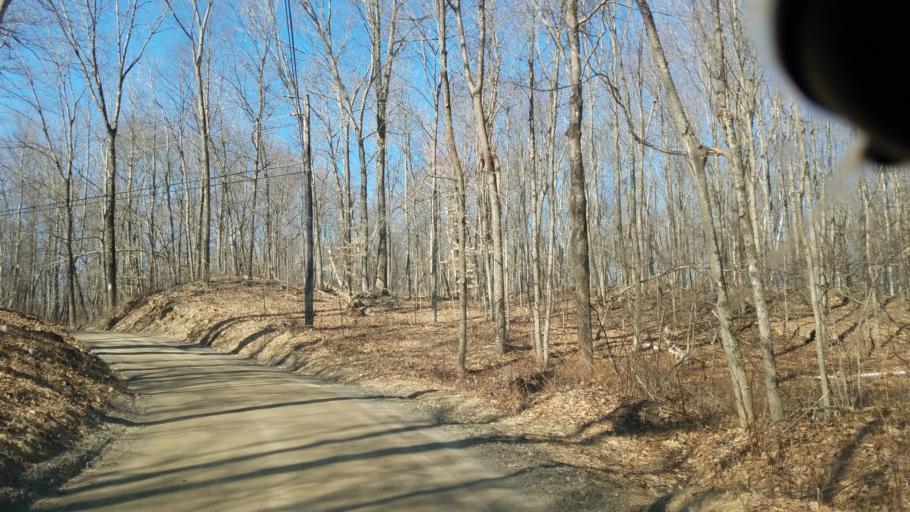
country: US
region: Connecticut
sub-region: Litchfield County
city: New Preston
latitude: 41.6252
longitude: -73.3394
